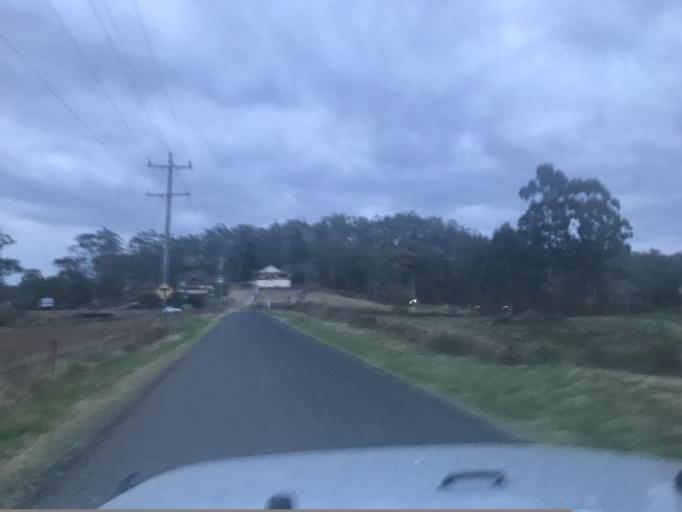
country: AU
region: New South Wales
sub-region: Hawkesbury
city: Pitt Town
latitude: -33.5021
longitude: 150.8774
